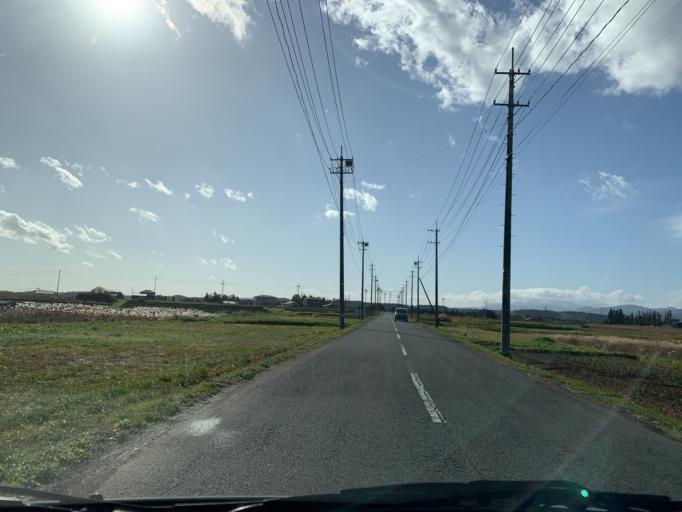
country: JP
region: Iwate
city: Mizusawa
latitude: 39.0589
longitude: 141.1178
